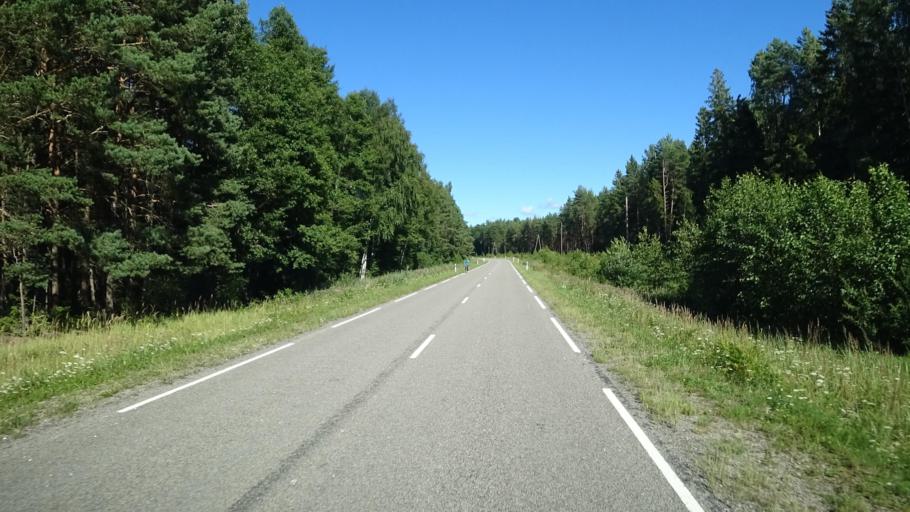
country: LV
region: Dundaga
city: Dundaga
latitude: 57.6769
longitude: 22.3395
